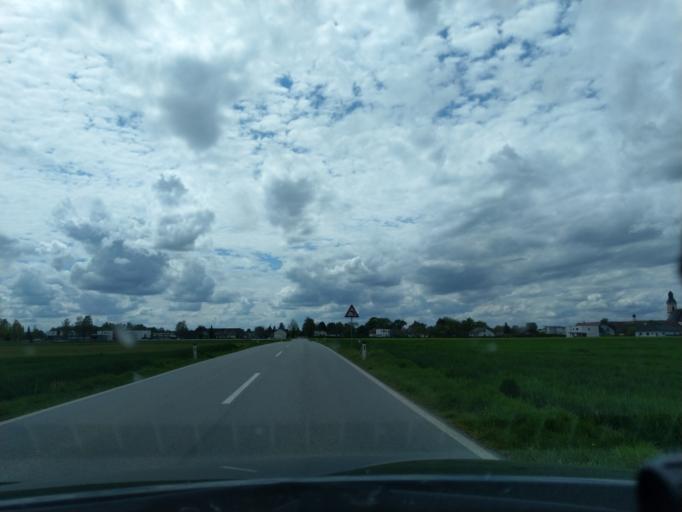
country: DE
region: Bavaria
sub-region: Lower Bavaria
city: Bad Fussing
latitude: 48.3385
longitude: 13.3697
